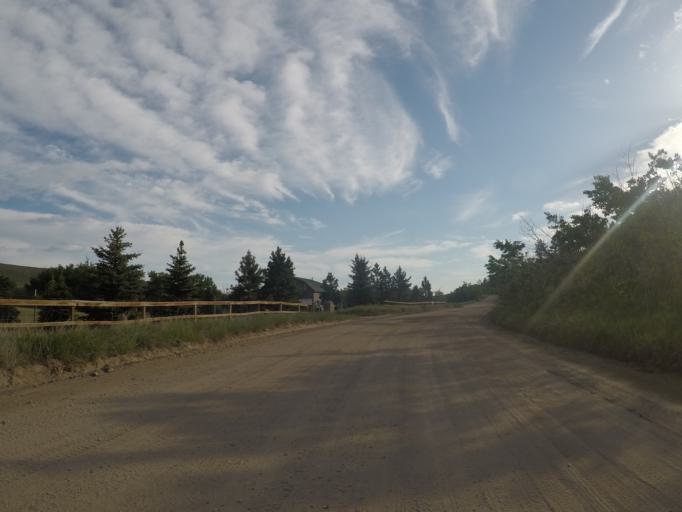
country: US
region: Montana
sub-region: Stillwater County
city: Absarokee
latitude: 45.3022
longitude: -109.5277
